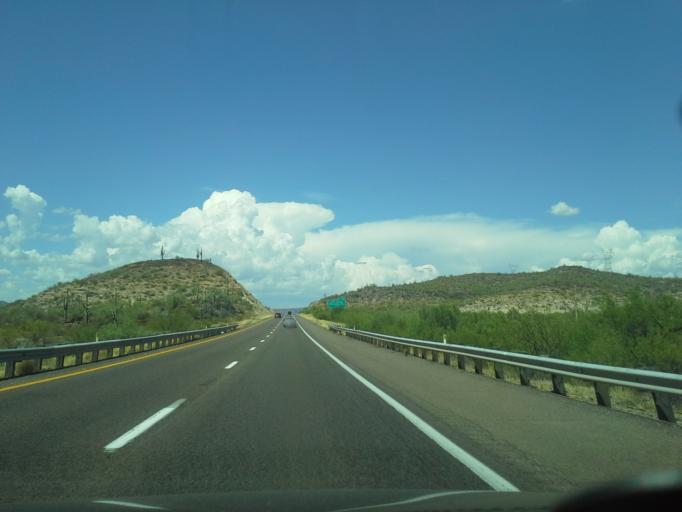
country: US
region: Arizona
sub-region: Yavapai County
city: Black Canyon City
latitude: 34.0321
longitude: -112.1456
